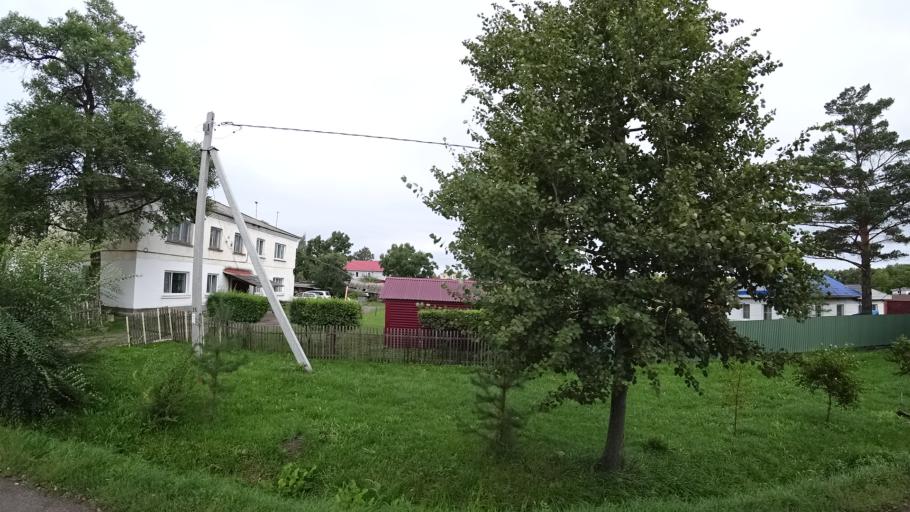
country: RU
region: Primorskiy
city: Chernigovka
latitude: 44.3381
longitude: 132.5805
